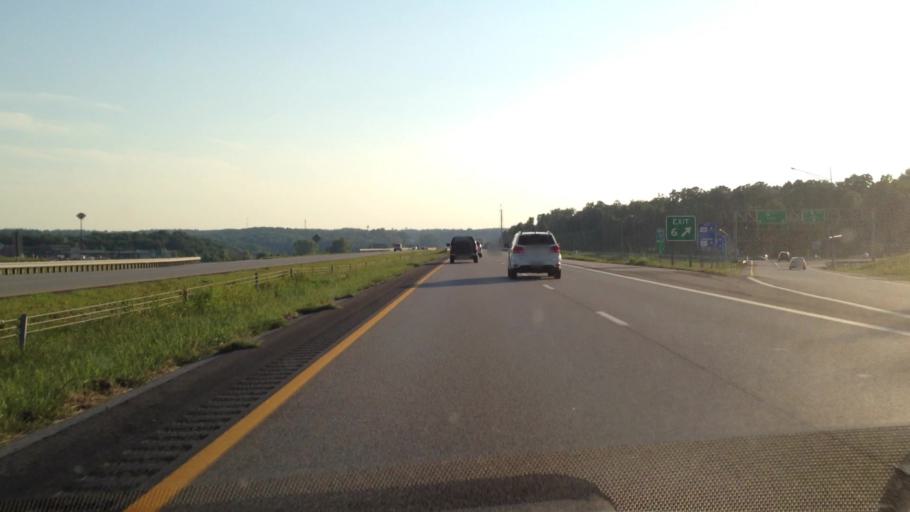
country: US
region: Missouri
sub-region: Jasper County
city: Joplin
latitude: 37.0382
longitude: -94.5119
